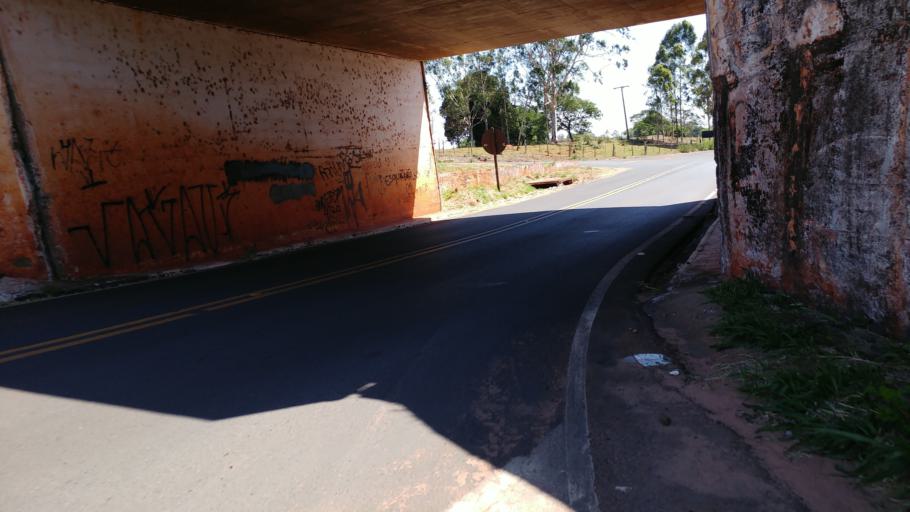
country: BR
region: Sao Paulo
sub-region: Paraguacu Paulista
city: Paraguacu Paulista
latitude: -22.4181
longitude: -50.5932
